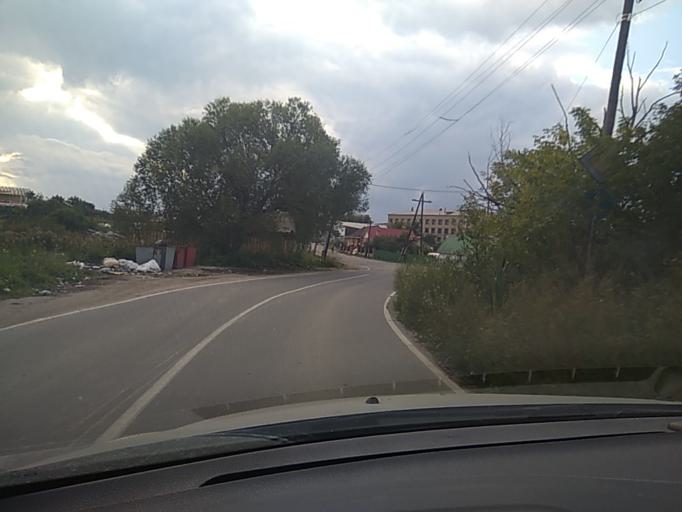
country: RU
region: Chelyabinsk
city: Kyshtym
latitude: 55.6972
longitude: 60.5430
